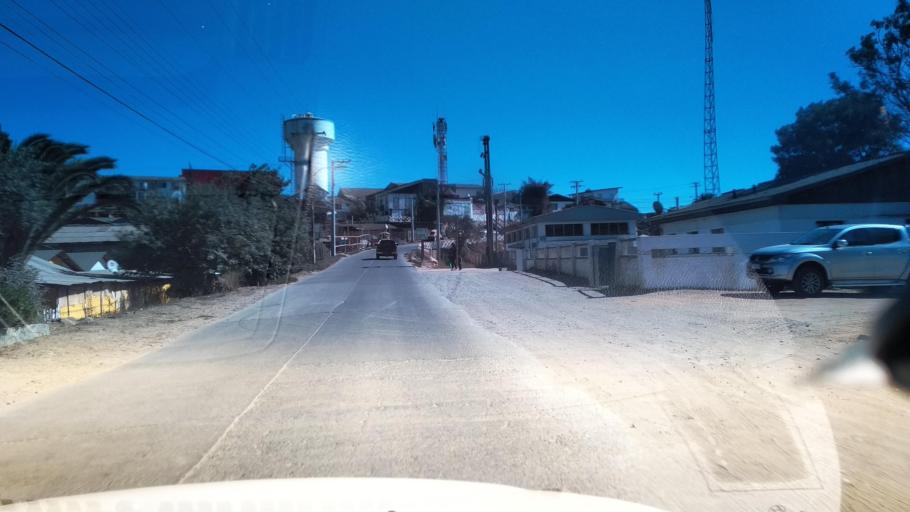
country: CL
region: O'Higgins
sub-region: Provincia de Colchagua
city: Santa Cruz
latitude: -34.3859
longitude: -72.0009
